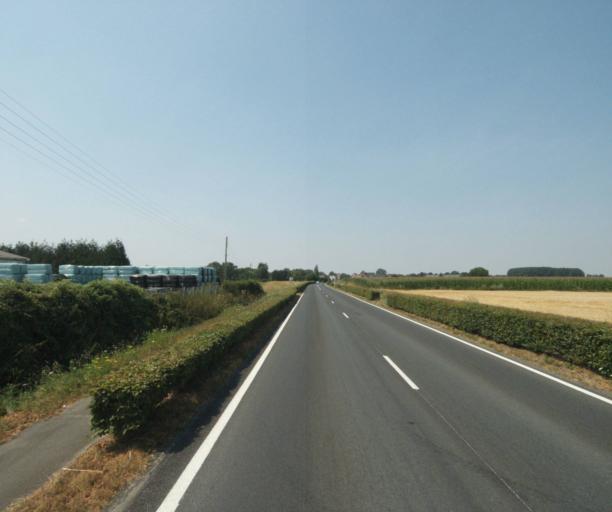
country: FR
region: Nord-Pas-de-Calais
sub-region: Departement du Nord
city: Wambrechies
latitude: 50.6961
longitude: 3.0343
